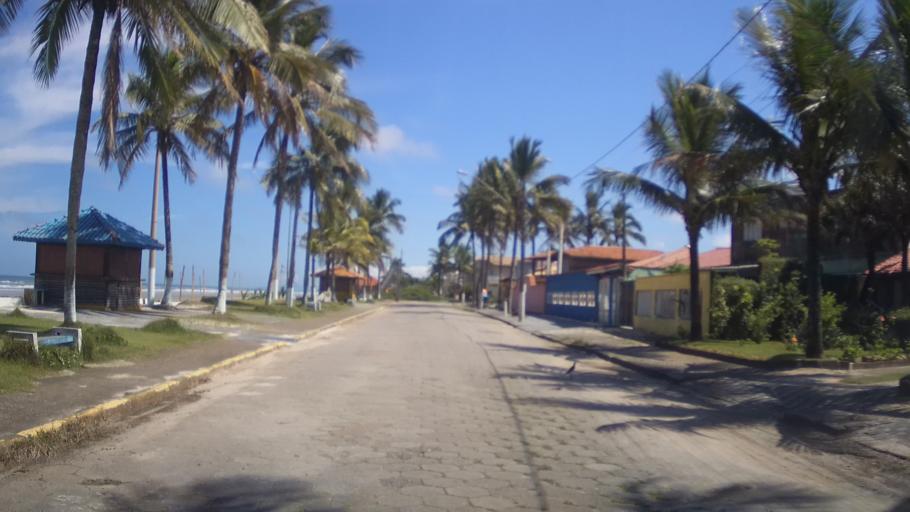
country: BR
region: Sao Paulo
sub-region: Itanhaem
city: Itanhaem
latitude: -24.1423
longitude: -46.7088
